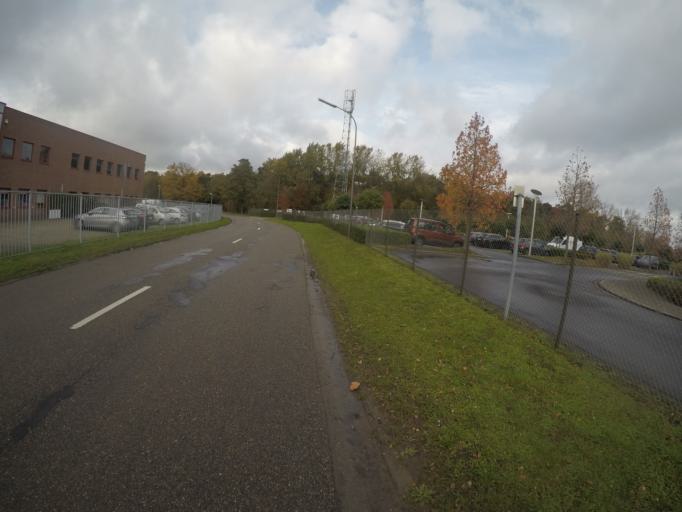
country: BE
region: Flanders
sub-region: Provincie Oost-Vlaanderen
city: Sint-Niklaas
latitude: 51.1423
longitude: 4.1616
